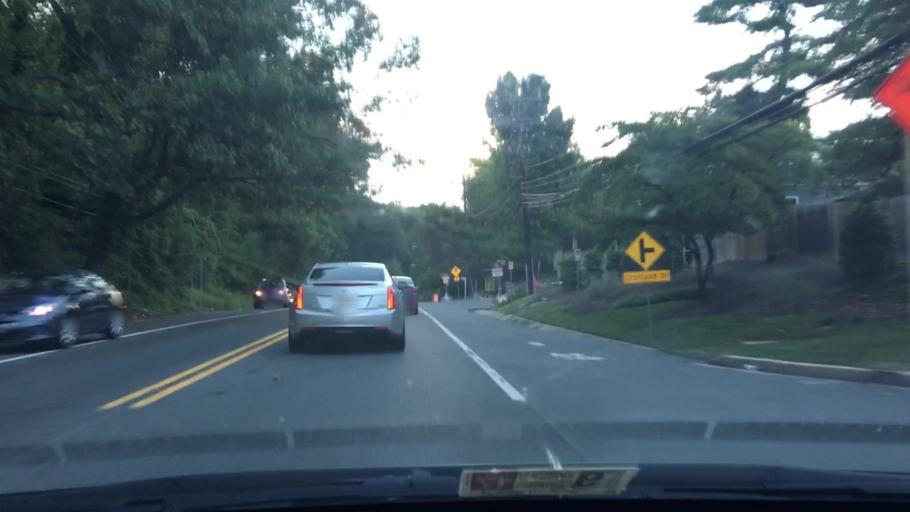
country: US
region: Maryland
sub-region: Montgomery County
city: North Bethesda
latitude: 39.0304
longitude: -77.1616
